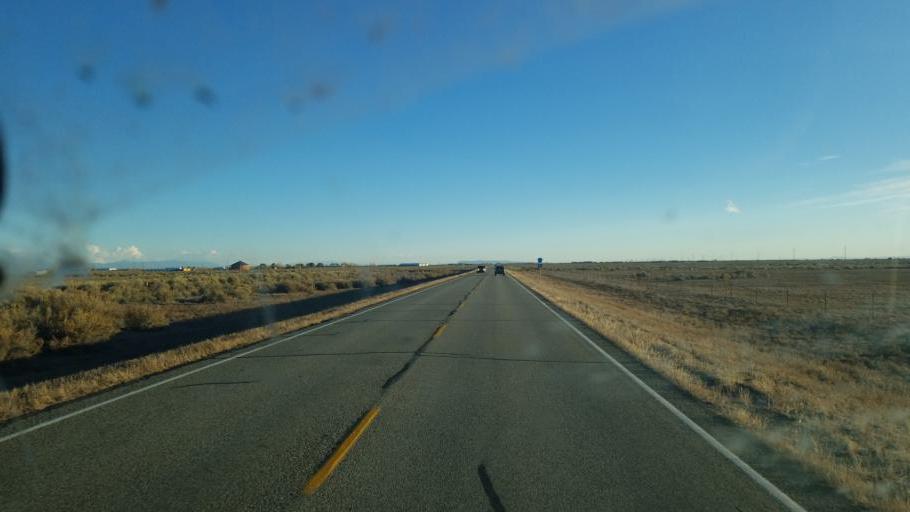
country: US
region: Colorado
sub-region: Saguache County
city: Center
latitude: 37.7235
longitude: -105.8781
